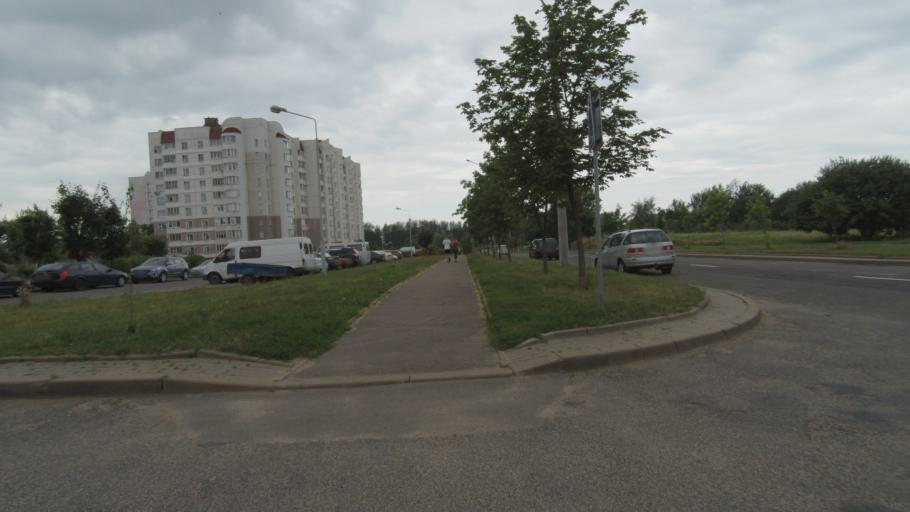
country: BY
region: Minsk
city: Syenitsa
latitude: 53.8494
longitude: 27.5622
